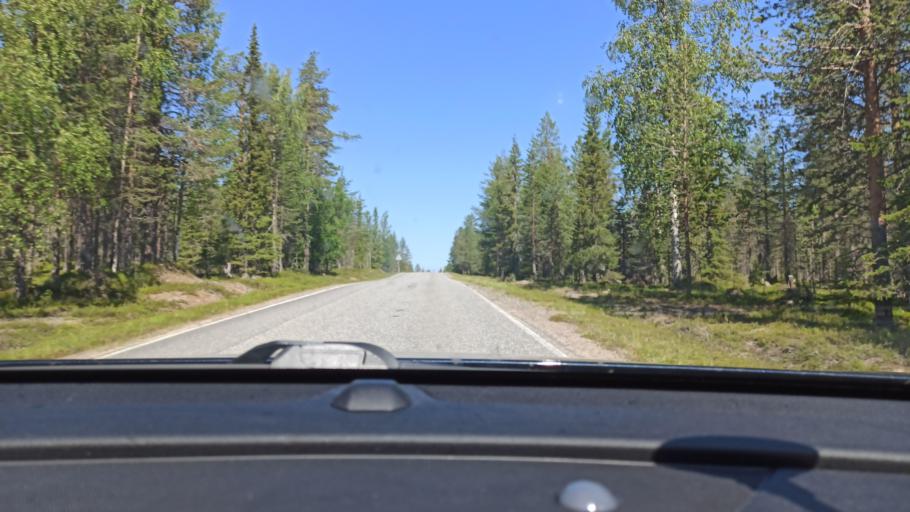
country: FI
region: Lapland
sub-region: Tunturi-Lappi
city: Kolari
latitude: 67.6795
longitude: 24.1396
